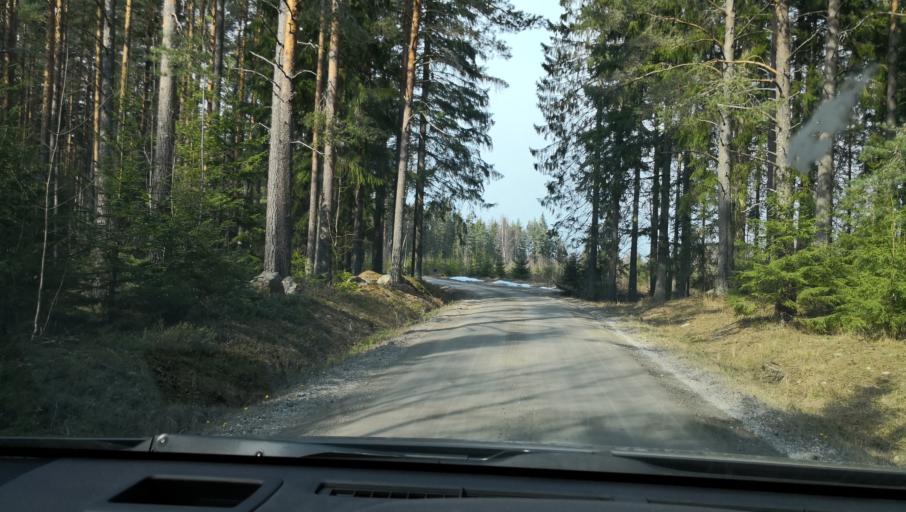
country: SE
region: OErebro
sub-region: Lindesbergs Kommun
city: Frovi
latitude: 59.3595
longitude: 15.4338
